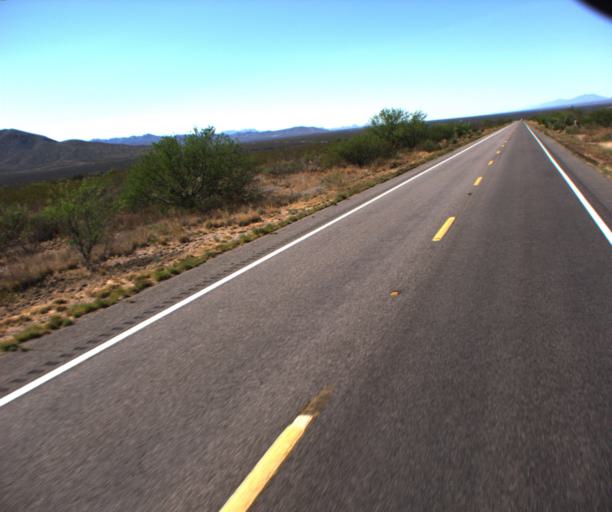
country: US
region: Arizona
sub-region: Cochise County
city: Tombstone
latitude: 31.6260
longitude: -110.0487
